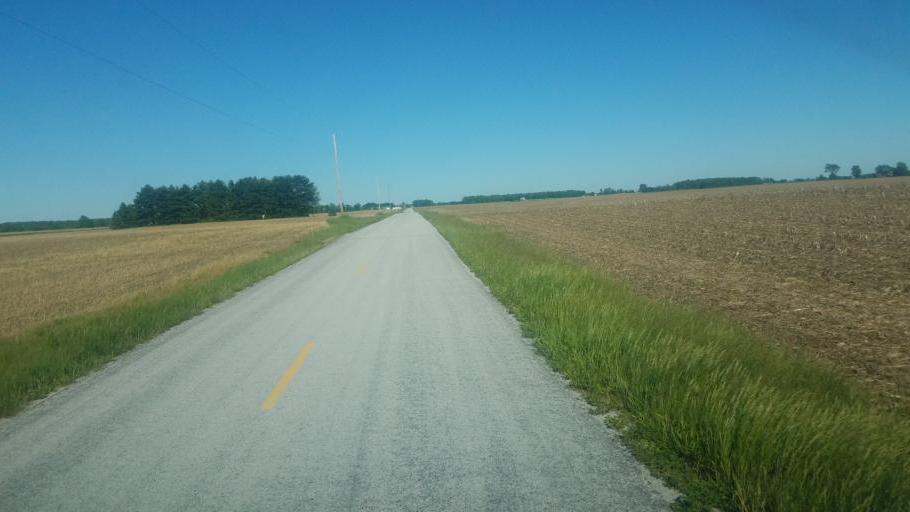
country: US
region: Ohio
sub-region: Hardin County
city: Kenton
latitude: 40.7026
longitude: -83.5557
